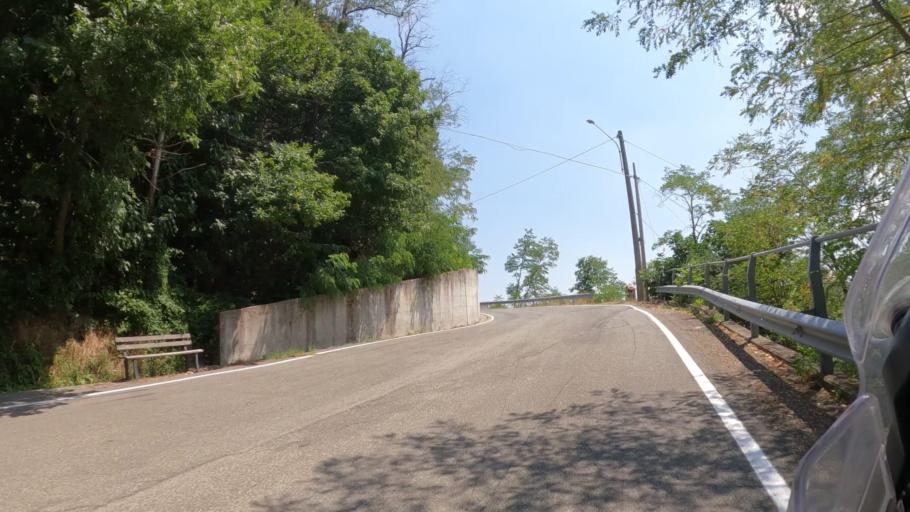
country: IT
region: Piedmont
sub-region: Provincia di Alessandria
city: Cassinelle-Concentrico
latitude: 44.5788
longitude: 8.5494
